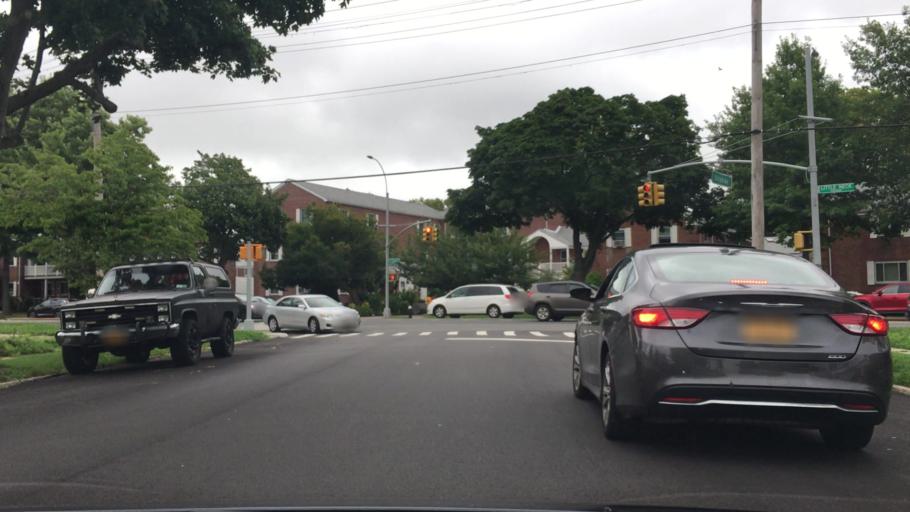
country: US
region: New York
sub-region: Nassau County
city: Bellerose
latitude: 40.7458
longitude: -73.7189
